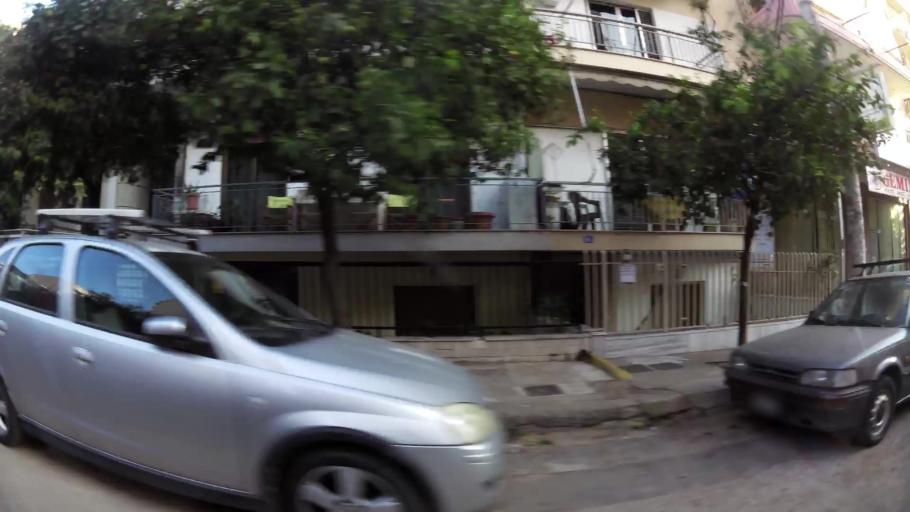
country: GR
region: Attica
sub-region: Nomos Piraios
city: Nikaia
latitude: 37.9714
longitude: 23.6392
